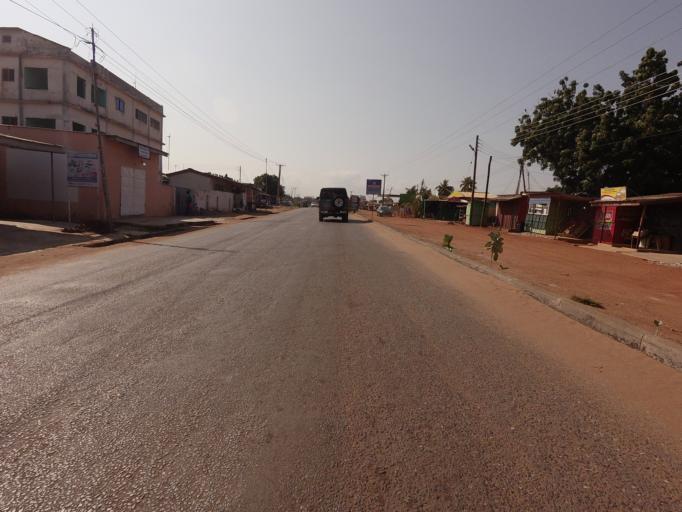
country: GH
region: Greater Accra
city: Teshi Old Town
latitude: 5.5992
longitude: -0.1028
